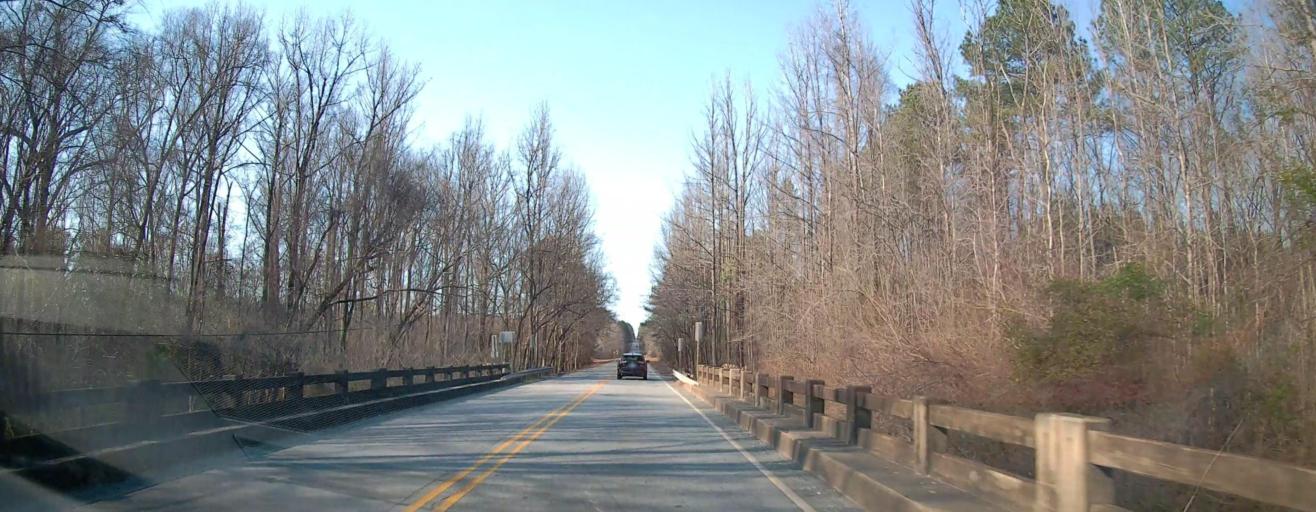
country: US
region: Georgia
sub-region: Butts County
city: Indian Springs
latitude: 33.1953
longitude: -83.8504
